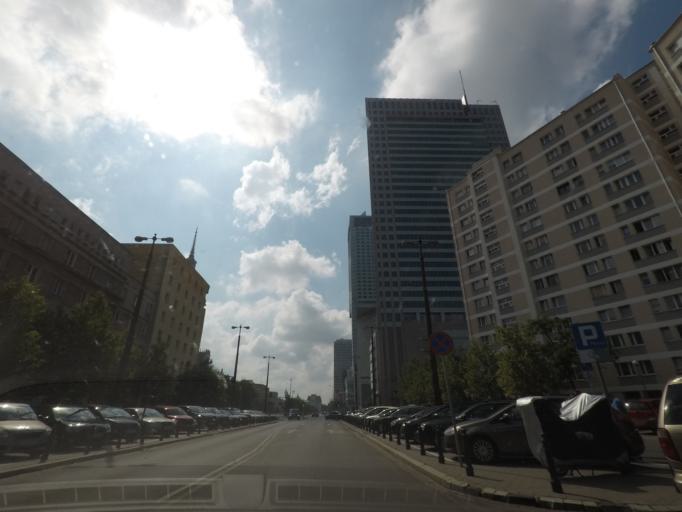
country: PL
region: Masovian Voivodeship
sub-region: Warszawa
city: Warsaw
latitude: 52.2348
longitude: 21.0017
